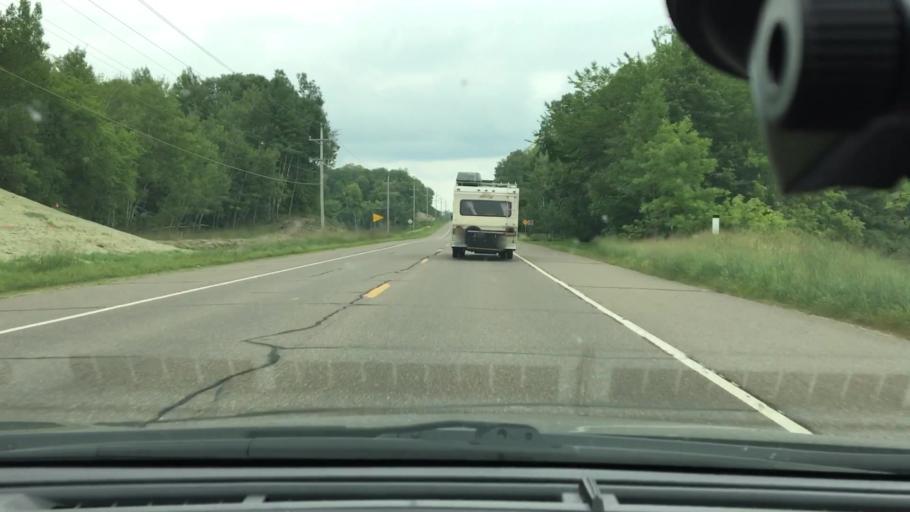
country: US
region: Minnesota
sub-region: Crow Wing County
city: Crosby
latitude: 46.4885
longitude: -93.9075
